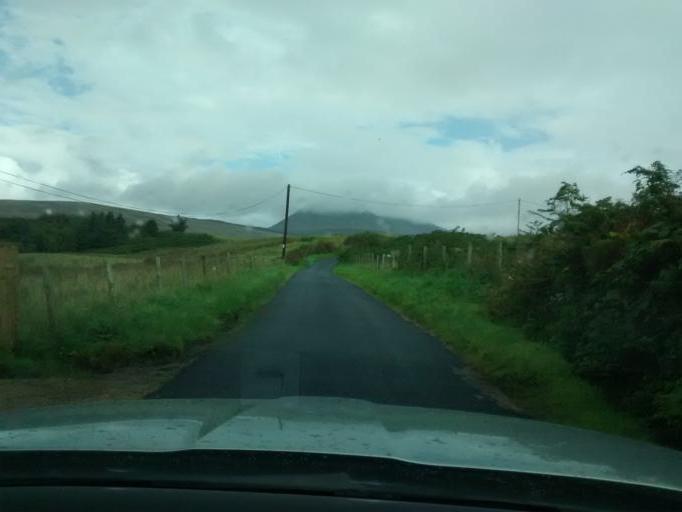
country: GB
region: Scotland
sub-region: North Ayrshire
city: Isle of Arran
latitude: 55.5723
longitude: -5.3480
